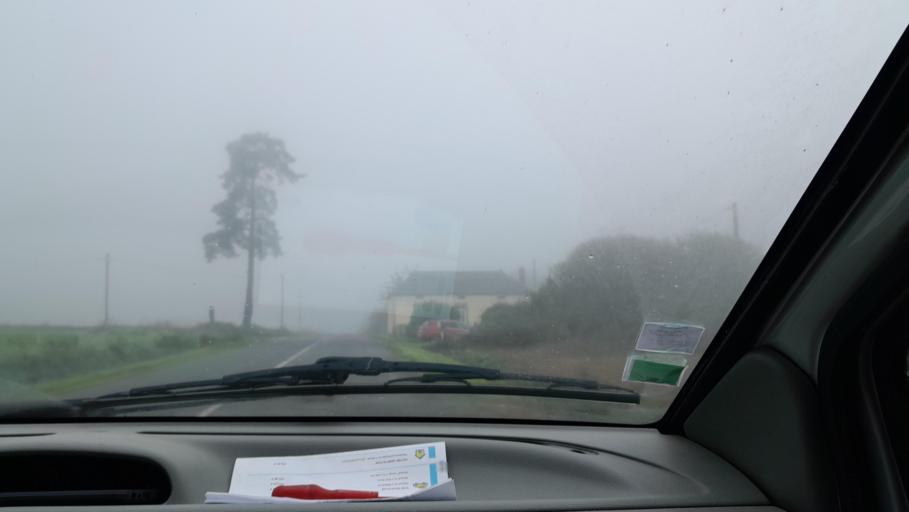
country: FR
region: Brittany
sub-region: Departement d'Ille-et-Vilaine
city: Le Pertre
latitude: 48.0161
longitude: -1.0379
